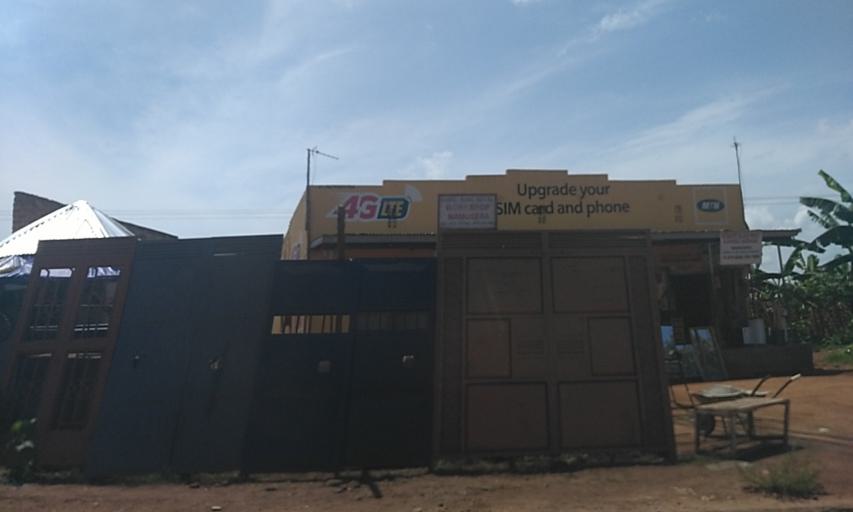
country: UG
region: Central Region
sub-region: Wakiso District
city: Wakiso
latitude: 0.4124
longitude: 32.4593
